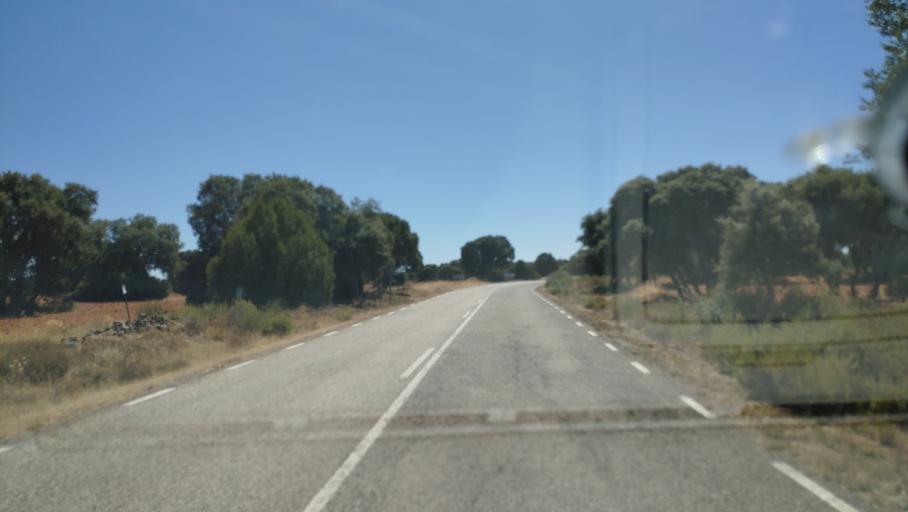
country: ES
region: Castille-La Mancha
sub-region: Provincia de Albacete
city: Ossa de Montiel
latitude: 38.8876
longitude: -2.7713
